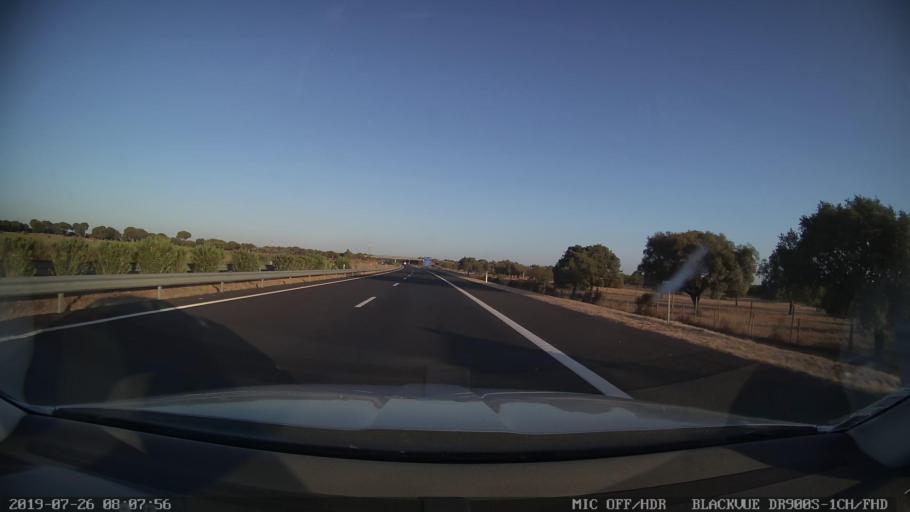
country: PT
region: Santarem
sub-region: Benavente
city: Benavente
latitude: 38.9278
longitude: -8.8153
